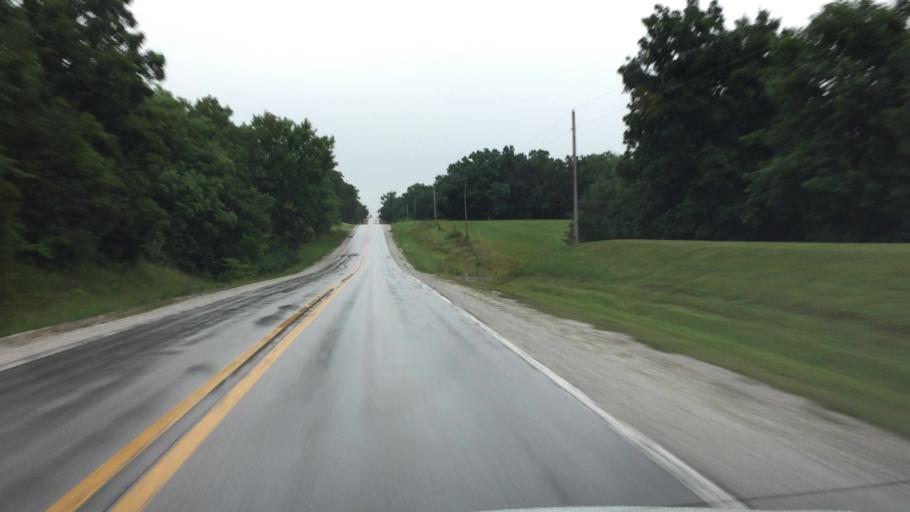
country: US
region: Illinois
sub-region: Hancock County
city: Carthage
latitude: 40.4352
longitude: -91.1401
